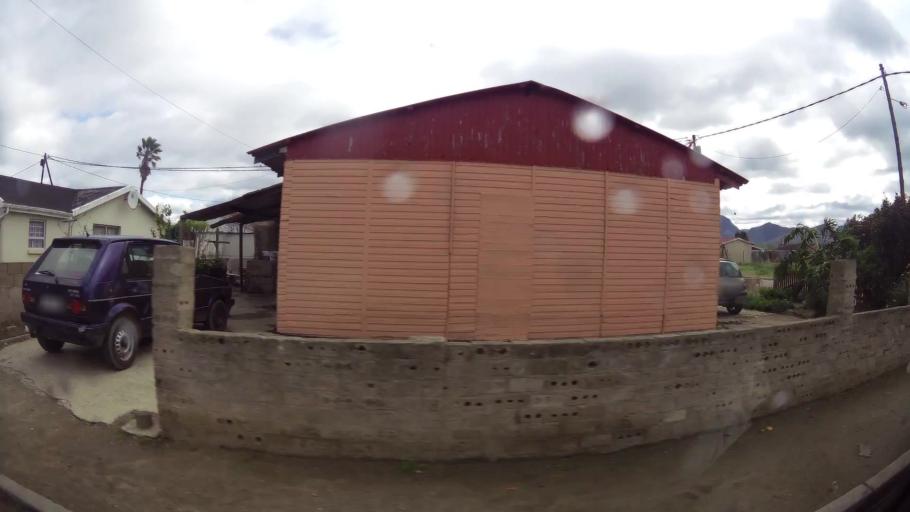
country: ZA
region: Western Cape
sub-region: Eden District Municipality
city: George
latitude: -33.9790
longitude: 22.4916
